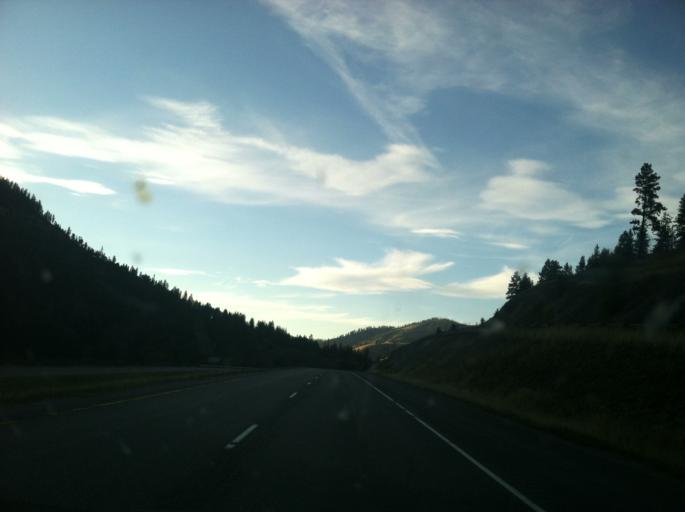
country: US
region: Montana
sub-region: Missoula County
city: Clinton
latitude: 46.7043
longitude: -113.5017
